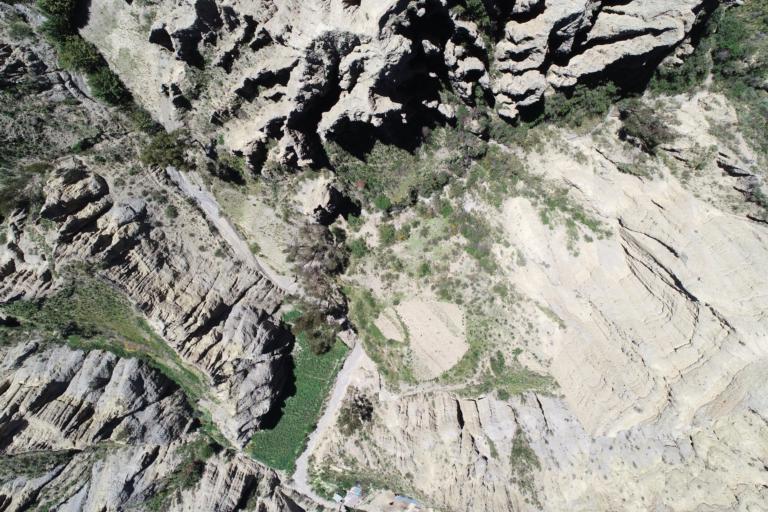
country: BO
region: La Paz
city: La Paz
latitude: -16.5052
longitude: -68.0643
